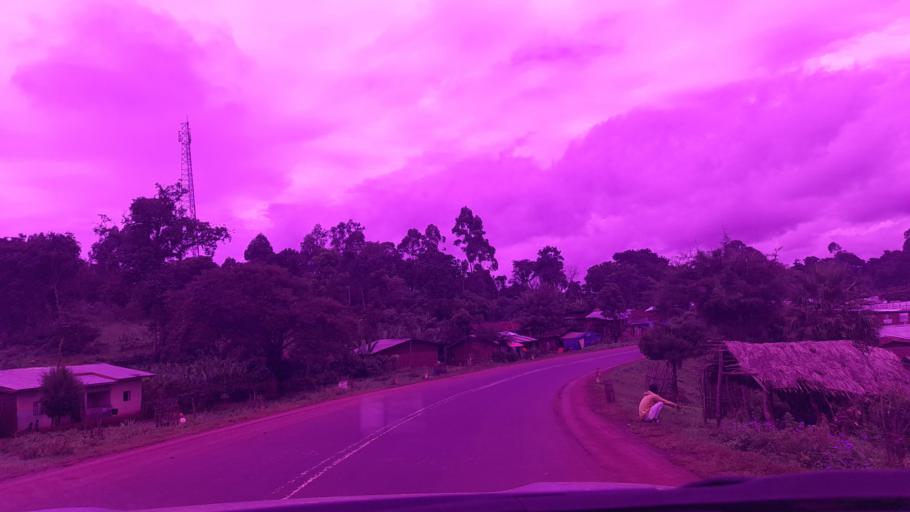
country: ET
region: Southern Nations, Nationalities, and People's Region
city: Bonga
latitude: 7.2951
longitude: 35.9869
